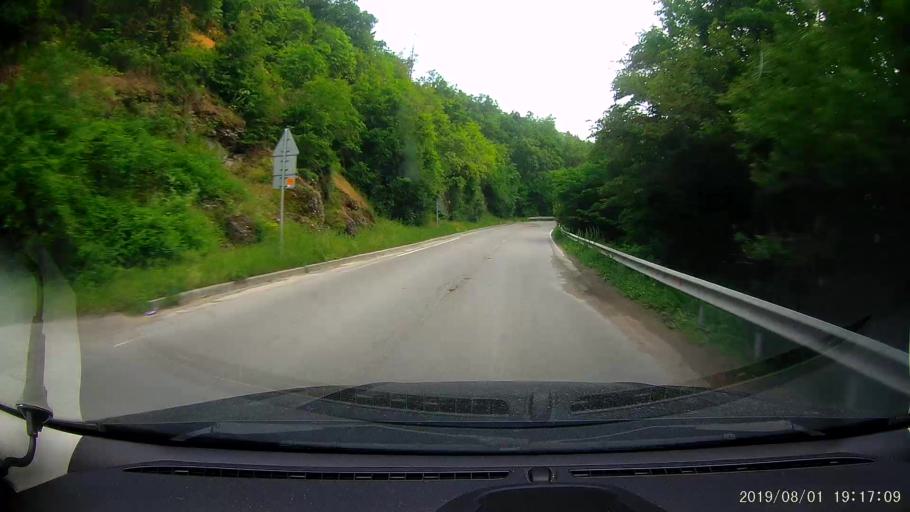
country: BG
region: Shumen
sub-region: Obshtina Smyadovo
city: Smyadovo
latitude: 42.9265
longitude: 26.9450
